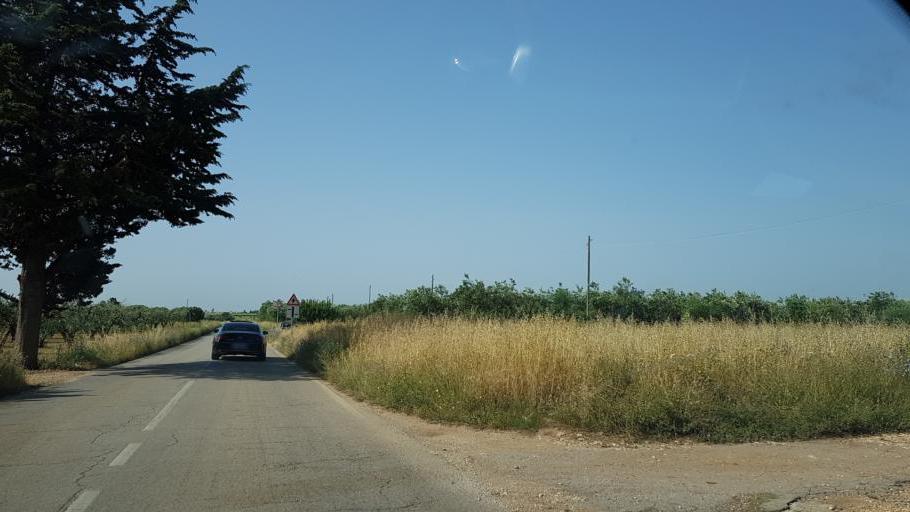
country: IT
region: Apulia
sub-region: Provincia di Brindisi
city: San Pancrazio Salentino
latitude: 40.4441
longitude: 17.8410
